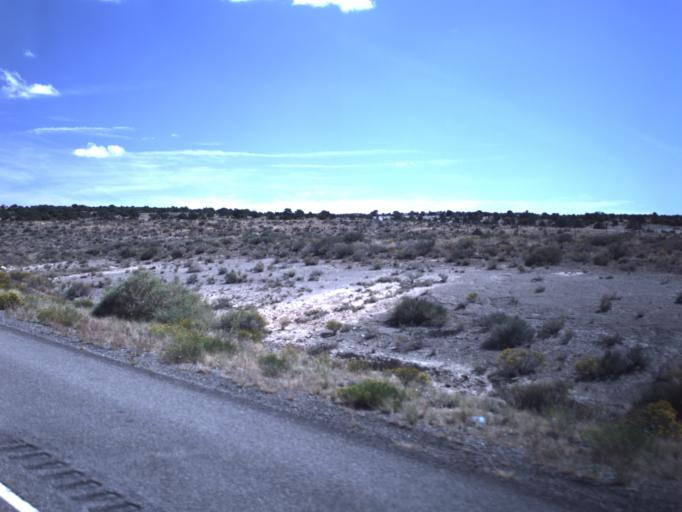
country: US
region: Utah
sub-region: Emery County
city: Ferron
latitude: 38.8419
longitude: -110.9658
